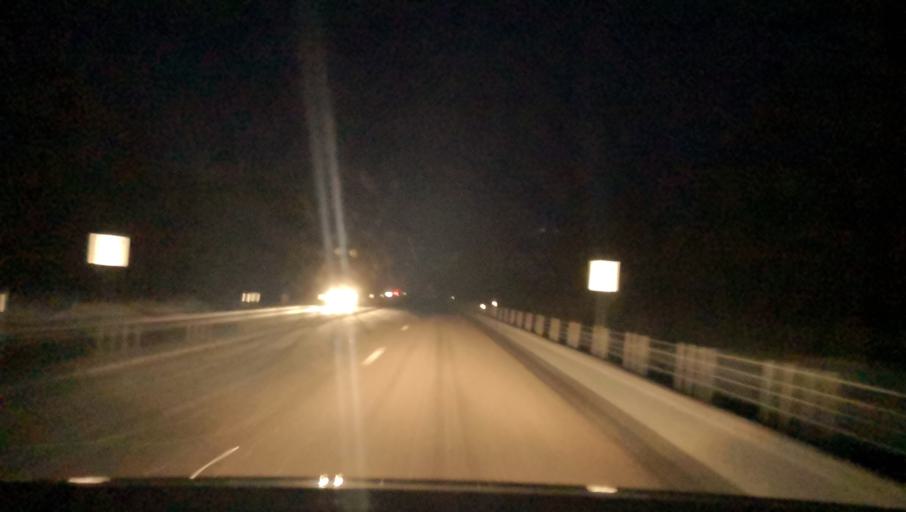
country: SE
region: Uppsala
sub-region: Heby Kommun
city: Tarnsjo
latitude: 60.2740
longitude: 16.9337
